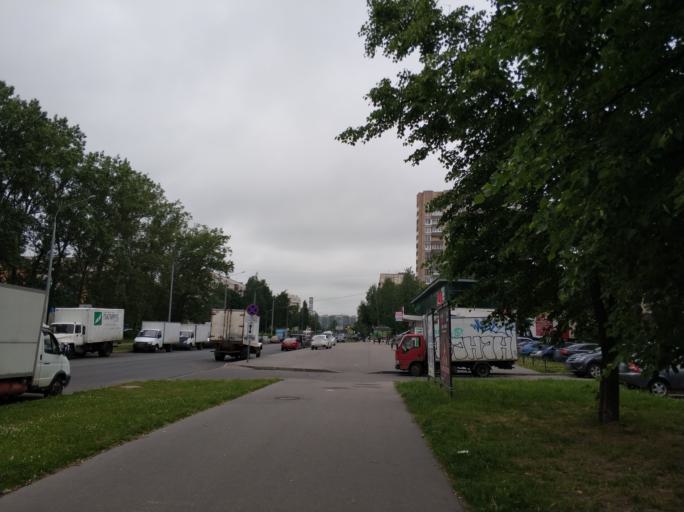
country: RU
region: St.-Petersburg
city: Grazhdanka
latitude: 60.0402
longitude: 30.4141
